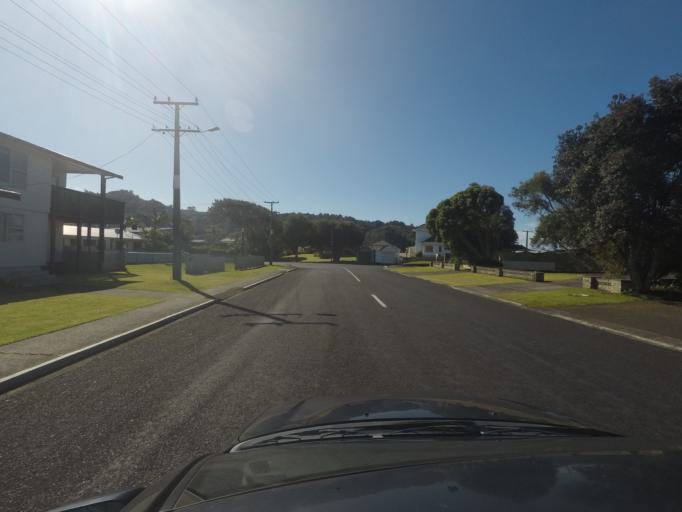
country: NZ
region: Bay of Plenty
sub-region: Western Bay of Plenty District
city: Waihi Beach
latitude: -37.4031
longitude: 175.9402
